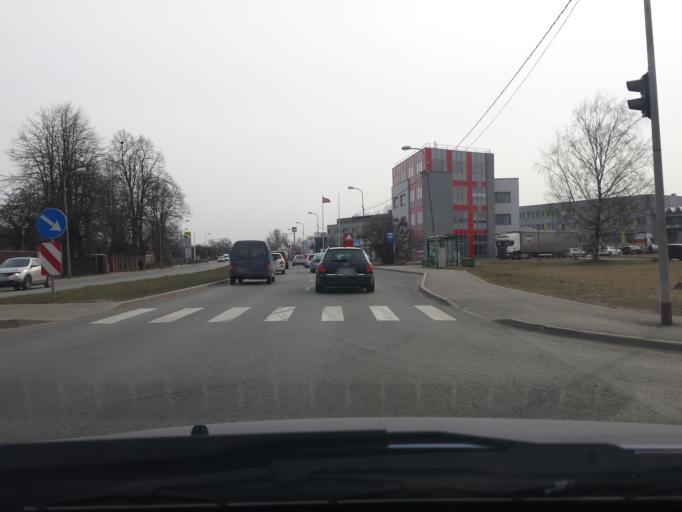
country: LV
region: Riga
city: Riga
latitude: 56.9419
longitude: 24.1817
